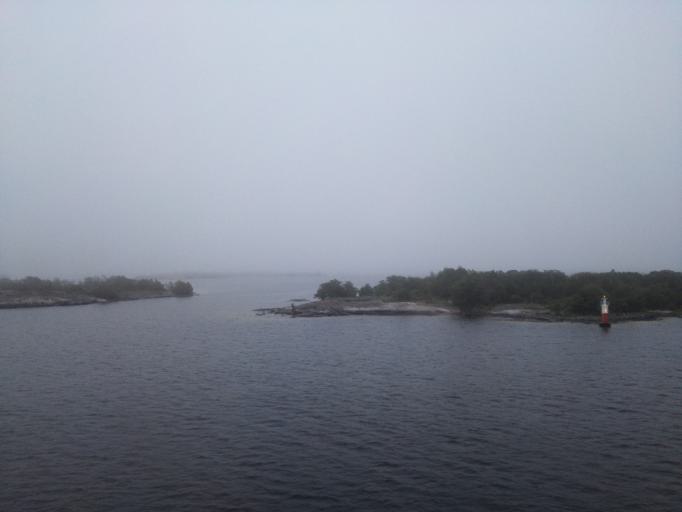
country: SE
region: Stockholm
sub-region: Norrtalje Kommun
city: Bjorko
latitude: 59.7394
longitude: 19.2349
